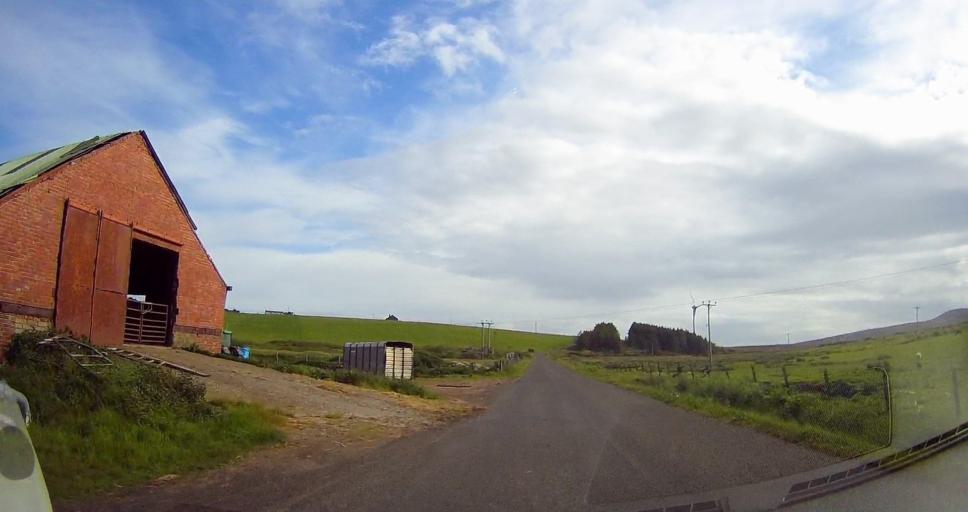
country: GB
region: Scotland
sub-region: Orkney Islands
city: Stromness
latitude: 58.8287
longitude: -3.2079
